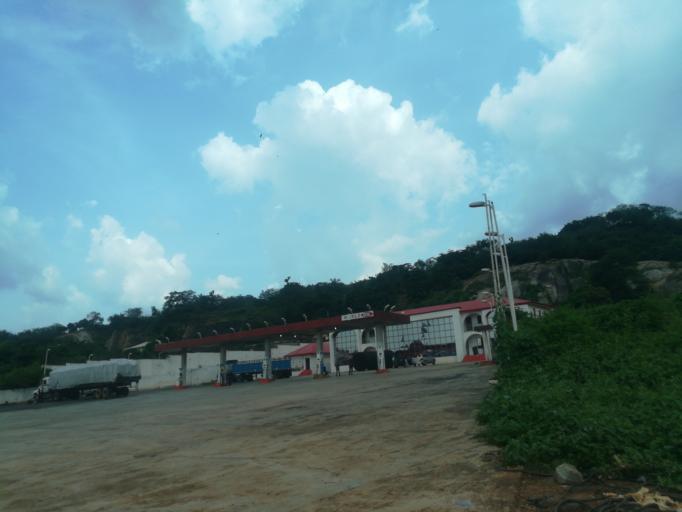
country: NG
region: Oyo
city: Moniya
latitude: 7.4839
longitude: 3.9166
